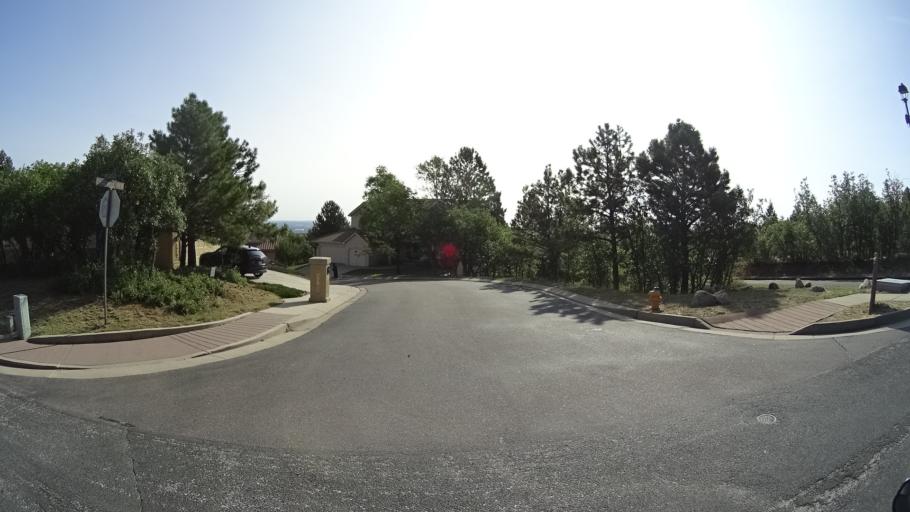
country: US
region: Colorado
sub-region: El Paso County
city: Colorado Springs
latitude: 38.8113
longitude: -104.8707
